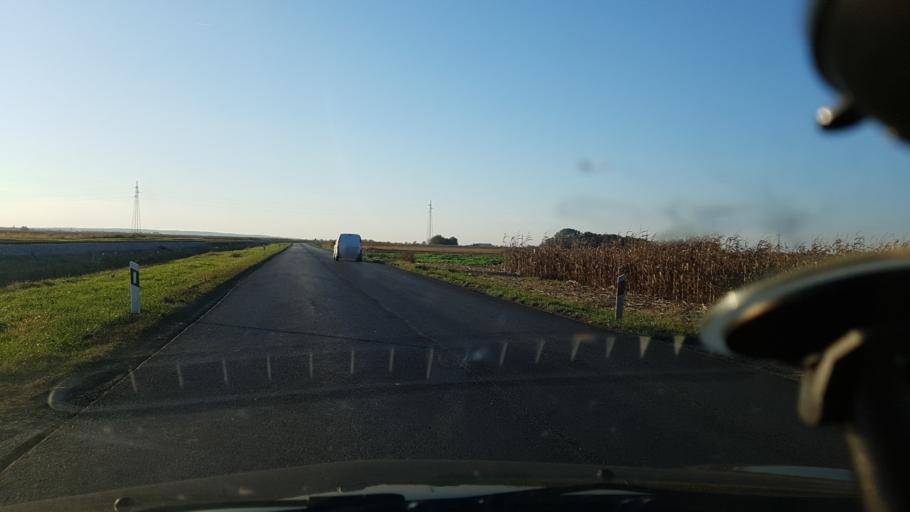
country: HR
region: Koprivnicko-Krizevacka
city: Virje
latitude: 46.0496
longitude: 17.0355
